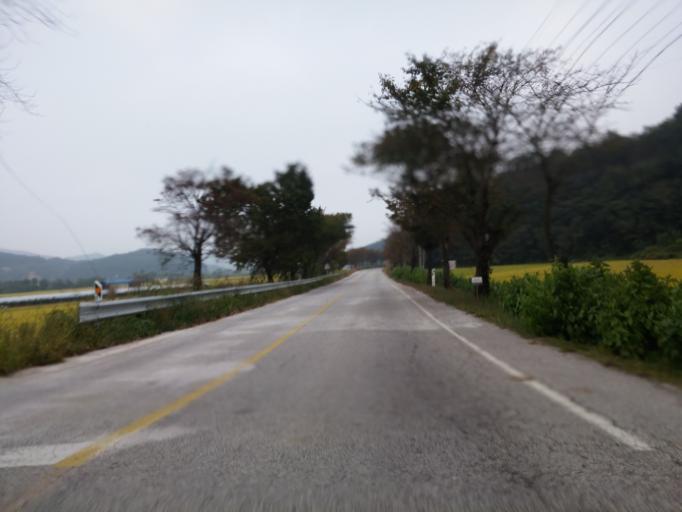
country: KR
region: Chungcheongbuk-do
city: Okcheon
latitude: 36.4143
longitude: 127.7676
